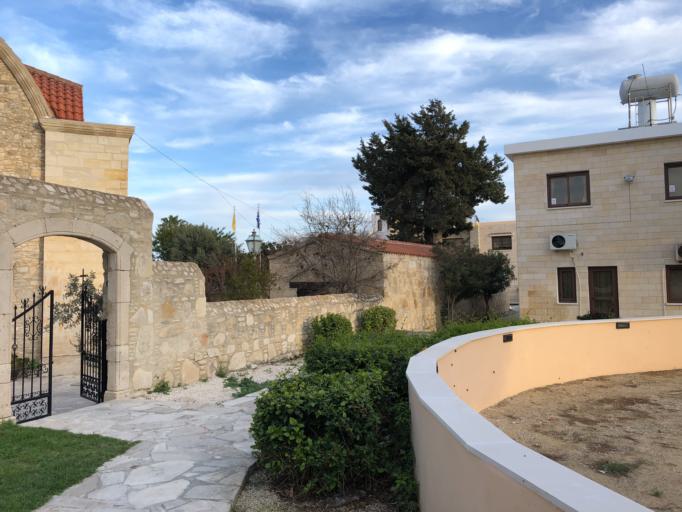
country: CY
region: Larnaka
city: Perivolia
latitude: 34.8287
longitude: 33.5789
